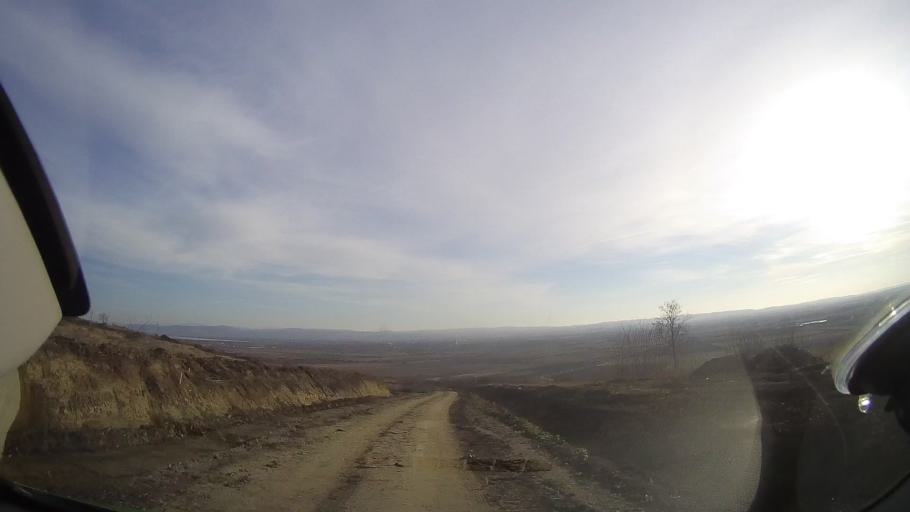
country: RO
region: Bihor
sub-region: Comuna Tileagd
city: Tileagd
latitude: 47.0981
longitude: 22.1770
